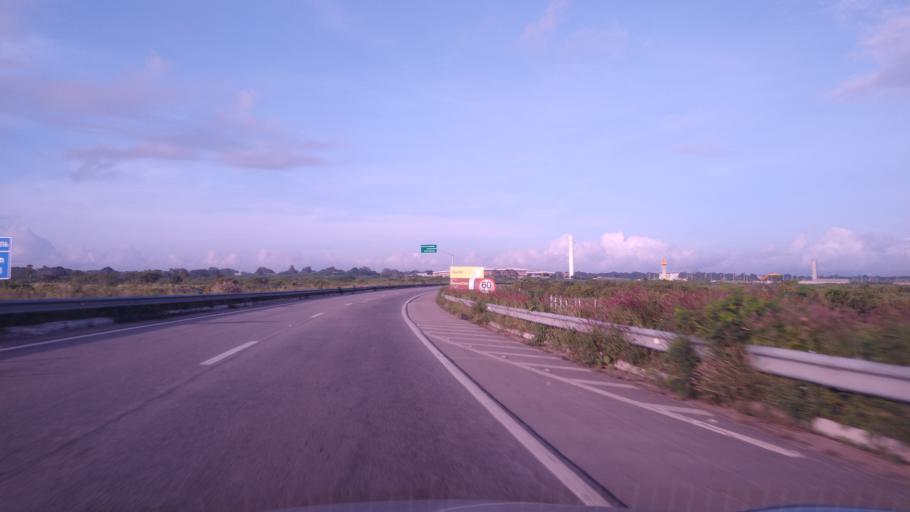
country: BR
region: Ceara
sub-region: Pacajus
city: Pacajus
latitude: -4.1601
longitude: -38.4838
